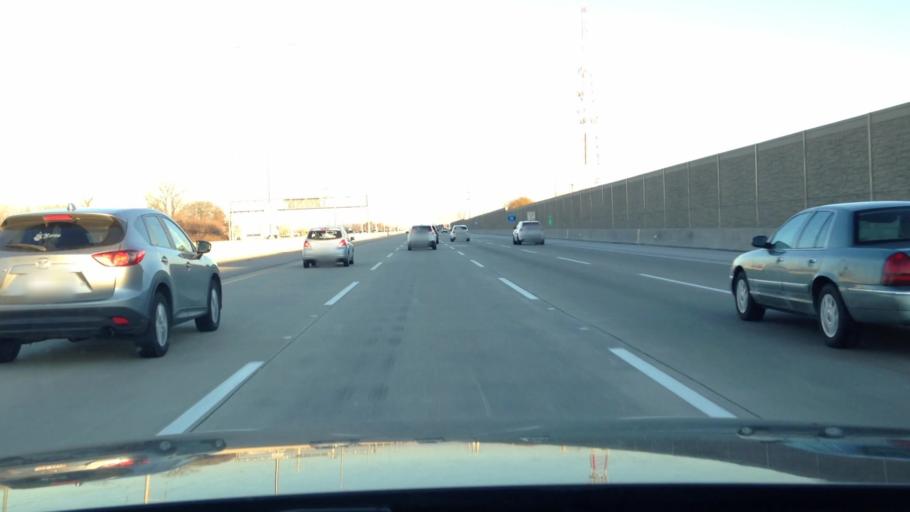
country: US
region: Illinois
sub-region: Kane County
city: East Dundee
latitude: 42.0655
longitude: -88.2467
